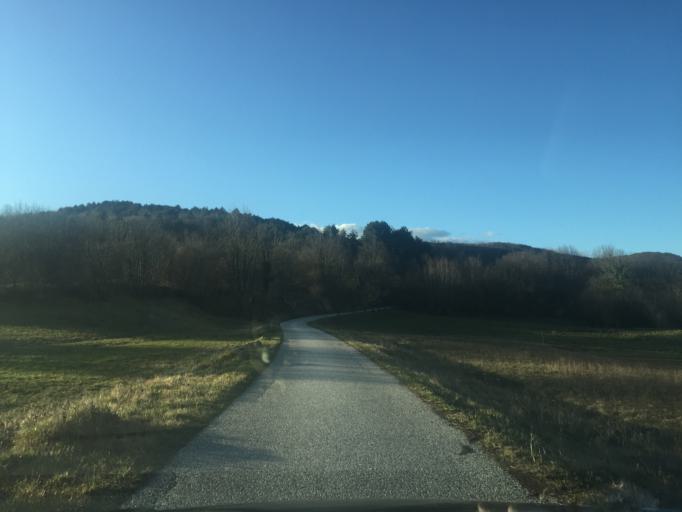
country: SI
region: Kanal
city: Deskle
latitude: 46.0338
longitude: 13.6662
